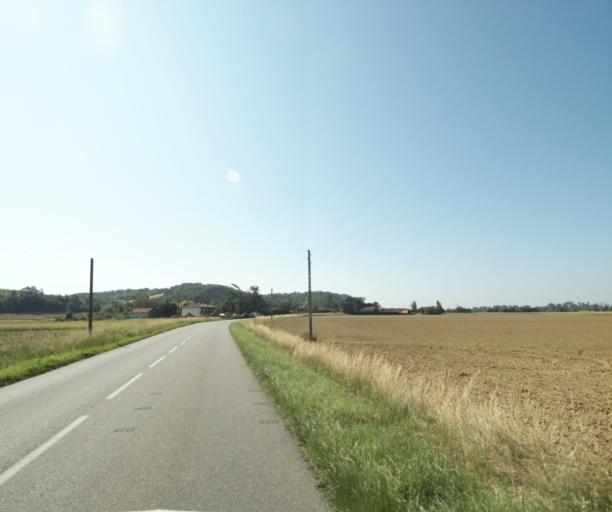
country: FR
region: Midi-Pyrenees
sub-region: Departement du Tarn-et-Garonne
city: Corbarieu
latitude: 43.9628
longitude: 1.3604
